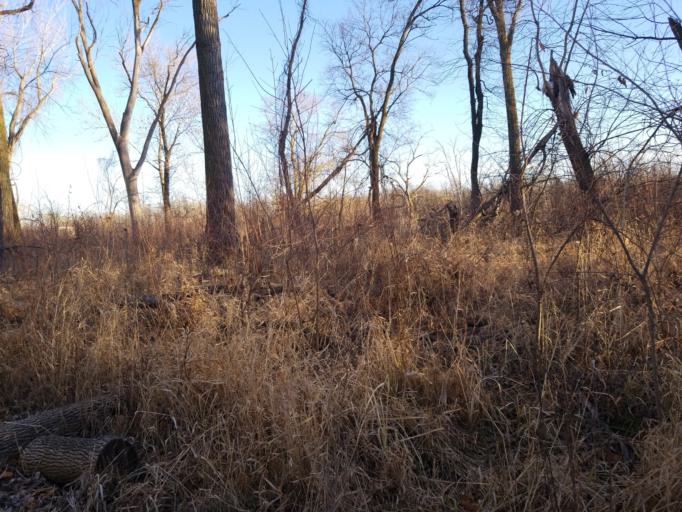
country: US
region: Nebraska
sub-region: Sarpy County
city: Bellevue
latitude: 41.1732
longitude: -95.8862
